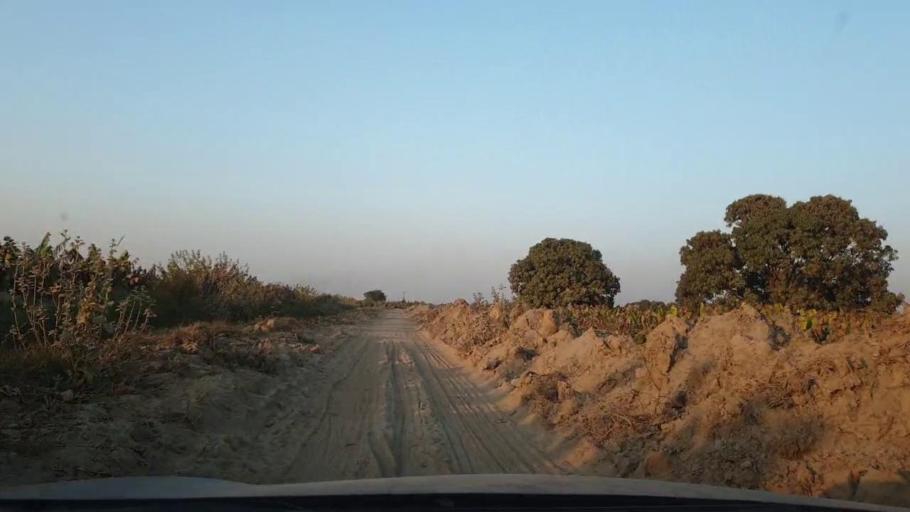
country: PK
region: Sindh
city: Tando Allahyar
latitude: 25.5298
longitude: 68.7363
